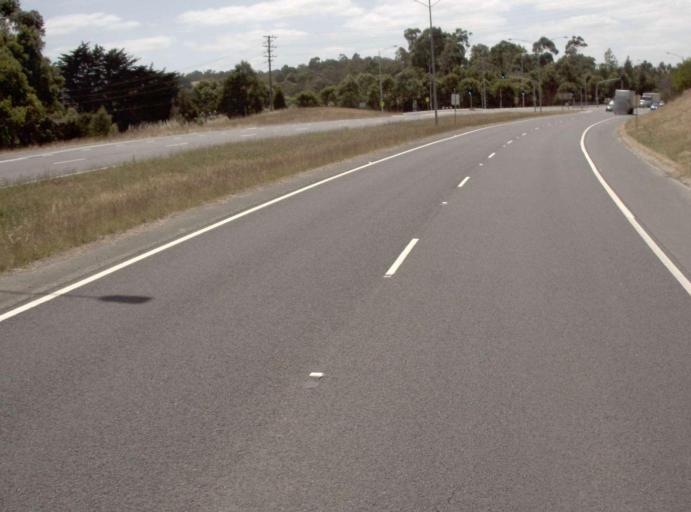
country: AU
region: Victoria
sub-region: Cardinia
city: Officer
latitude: -38.0560
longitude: 145.3797
